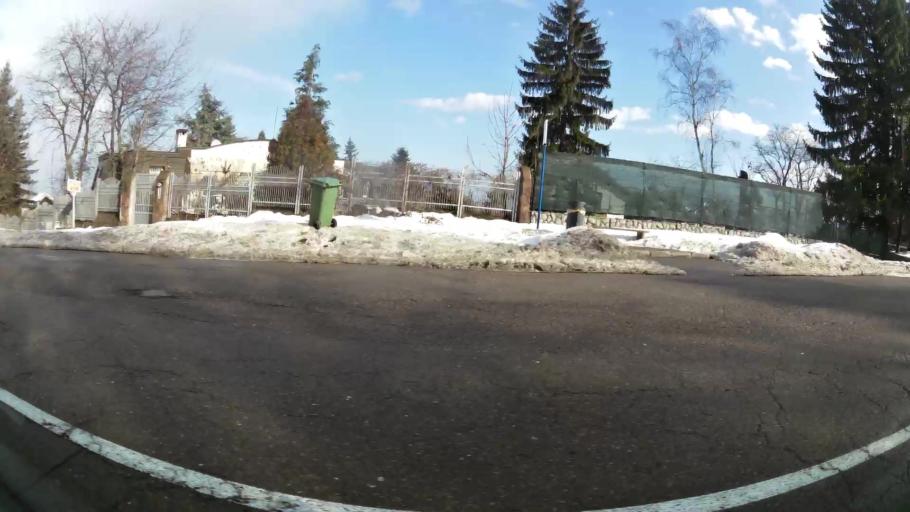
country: BG
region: Sofia-Capital
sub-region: Stolichna Obshtina
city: Sofia
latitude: 42.6473
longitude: 23.2471
